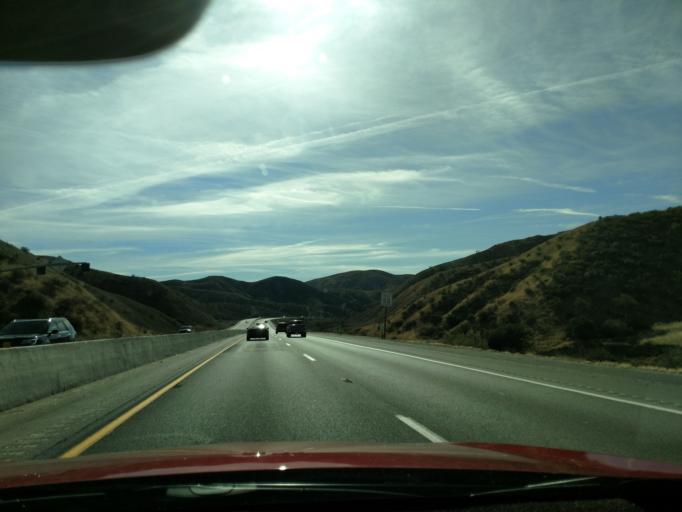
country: US
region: California
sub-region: Riverside County
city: Beaumont
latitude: 33.8809
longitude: -116.9912
